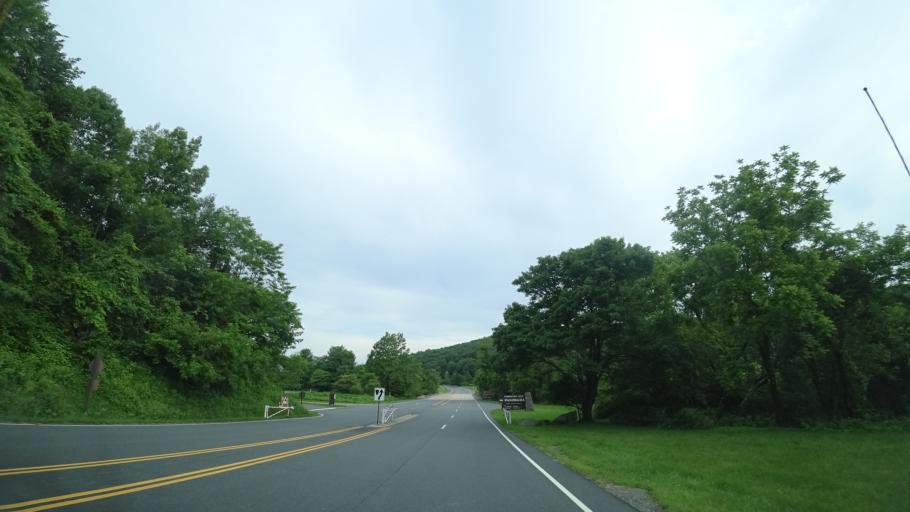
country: US
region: Virginia
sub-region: Page County
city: Luray
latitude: 38.6595
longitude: -78.3194
